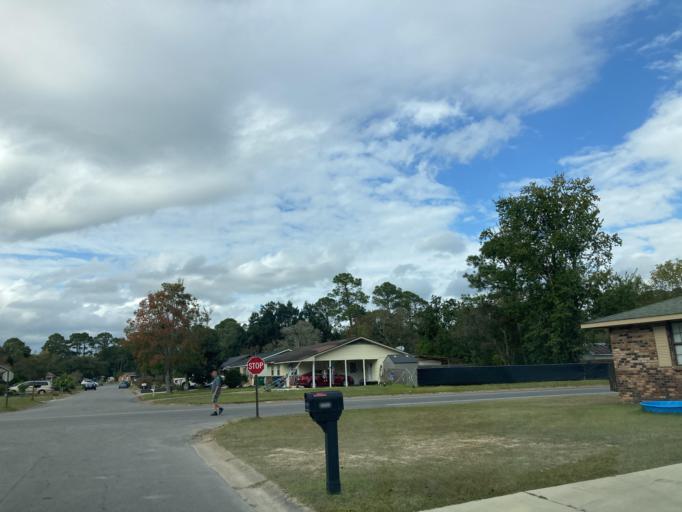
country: US
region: Mississippi
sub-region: Jackson County
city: Gulf Hills
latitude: 30.4356
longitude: -88.8265
